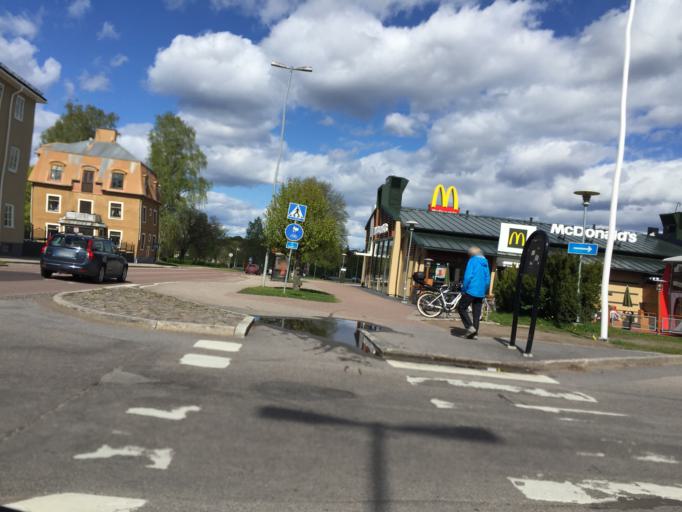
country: SE
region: Dalarna
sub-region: Ludvika Kommun
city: Ludvika
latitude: 60.1510
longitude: 15.1898
